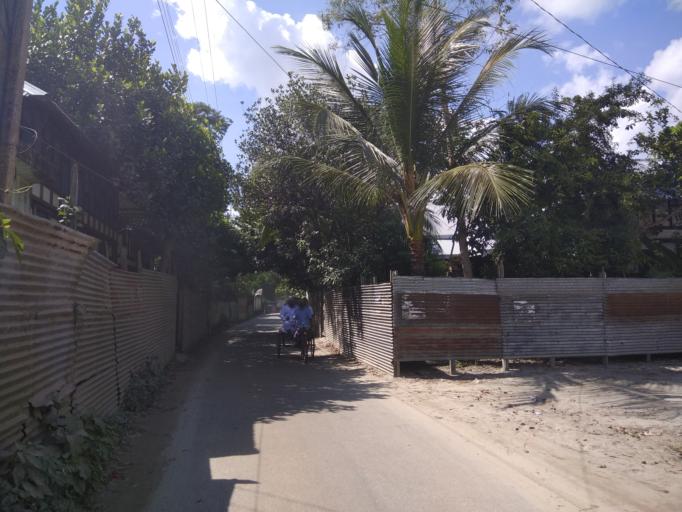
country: BD
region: Dhaka
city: Narayanganj
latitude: 23.4405
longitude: 90.4852
